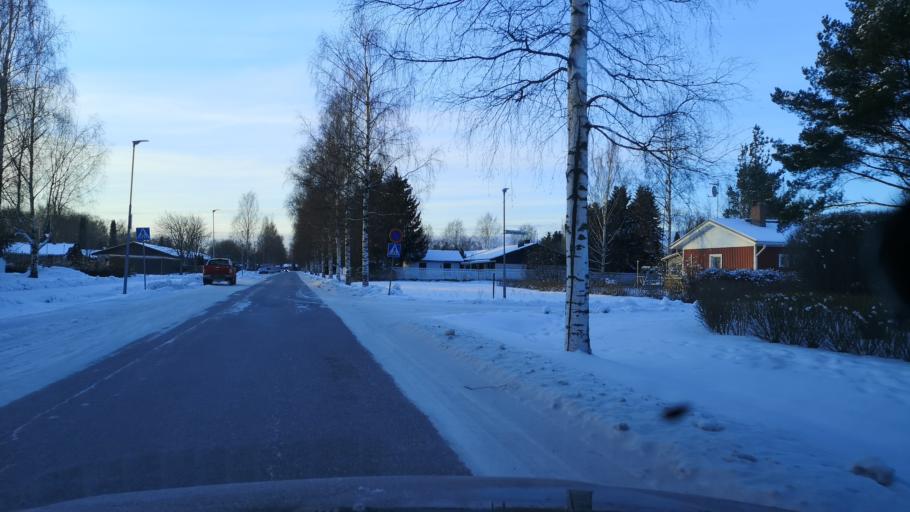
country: FI
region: Satakunta
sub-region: Pori
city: Pori
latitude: 61.5040
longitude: 21.8225
